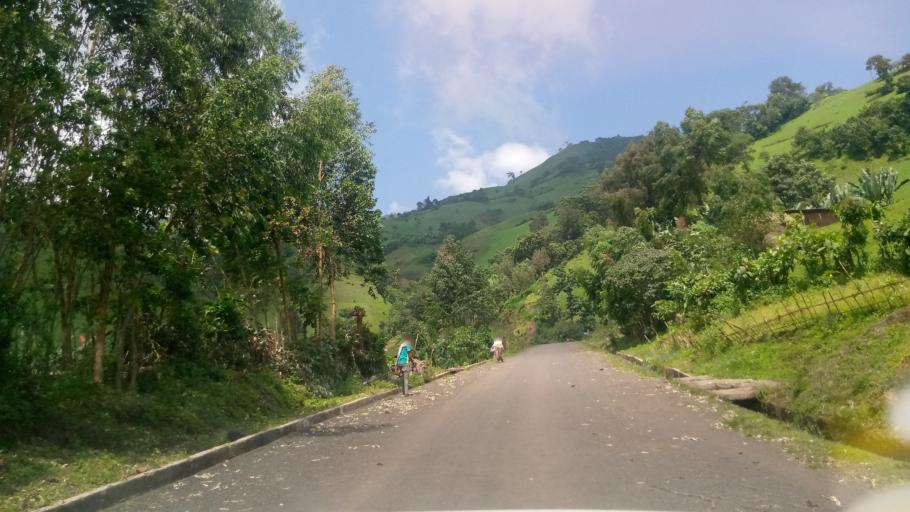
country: ET
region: Southern Nations, Nationalities, and People's Region
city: Bonga
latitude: 7.1457
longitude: 36.5738
